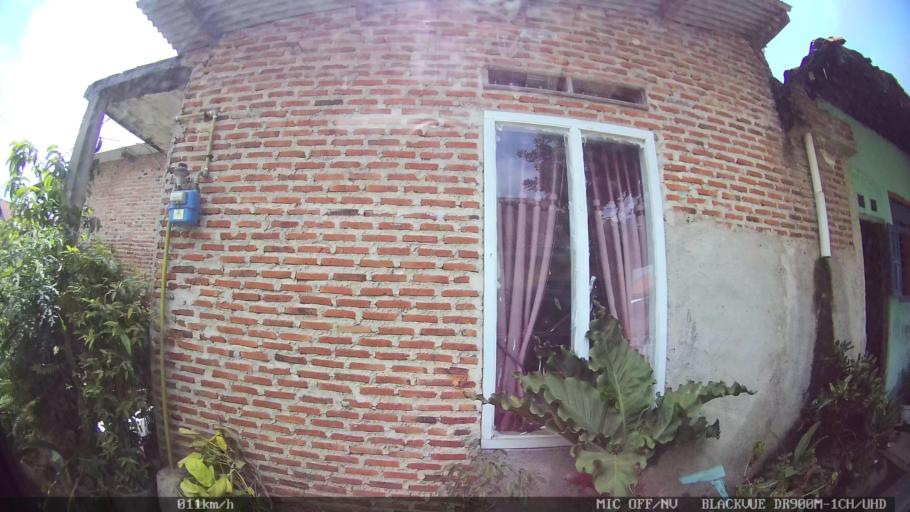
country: ID
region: Lampung
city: Kedaton
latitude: -5.3707
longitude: 105.3057
